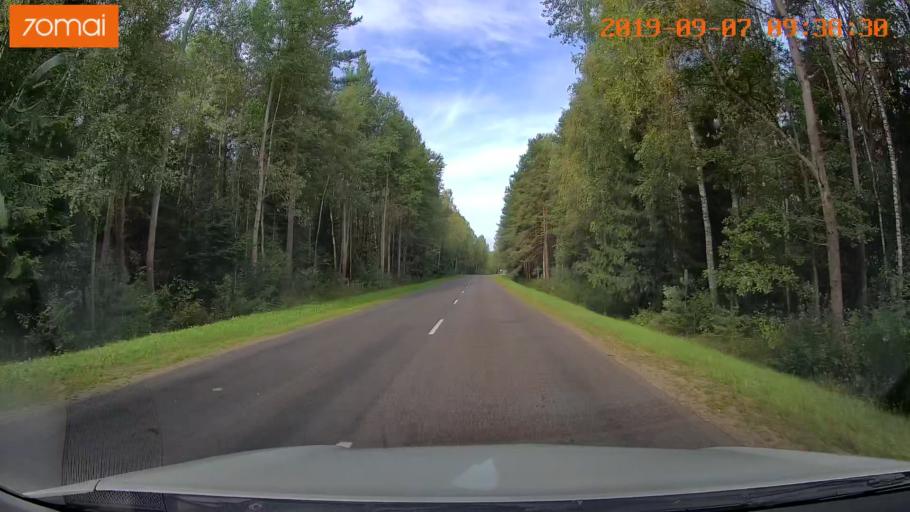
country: BY
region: Grodnenskaya
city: Iwye
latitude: 53.9244
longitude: 25.8196
